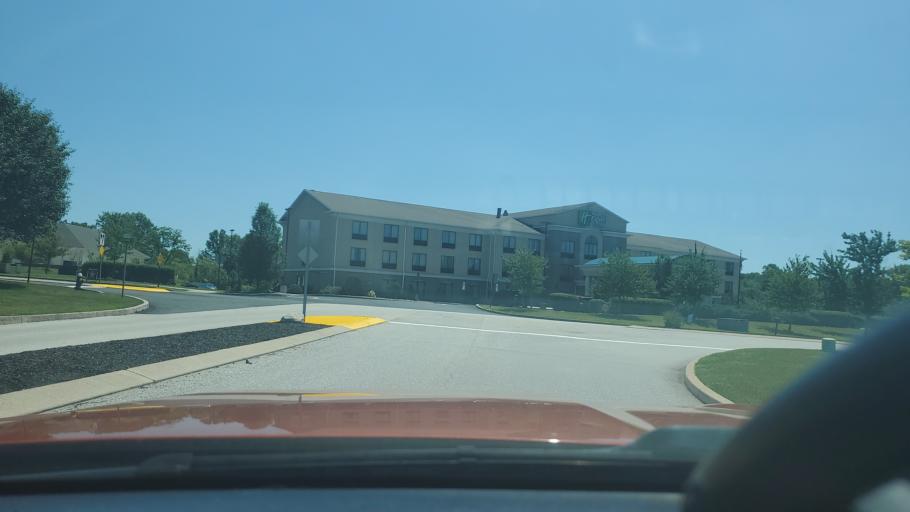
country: US
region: Pennsylvania
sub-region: Montgomery County
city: Limerick
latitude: 40.2168
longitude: -75.5515
